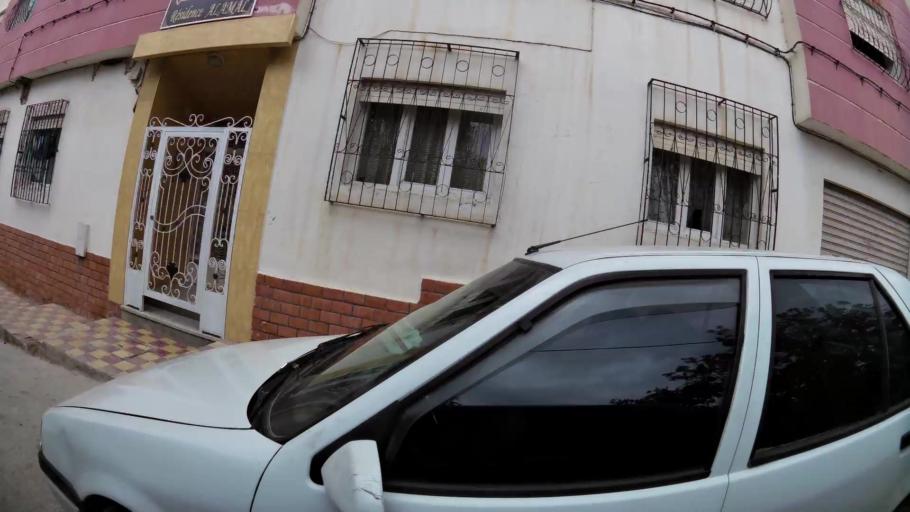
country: MA
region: Tanger-Tetouan
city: Tetouan
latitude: 35.5669
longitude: -5.3785
